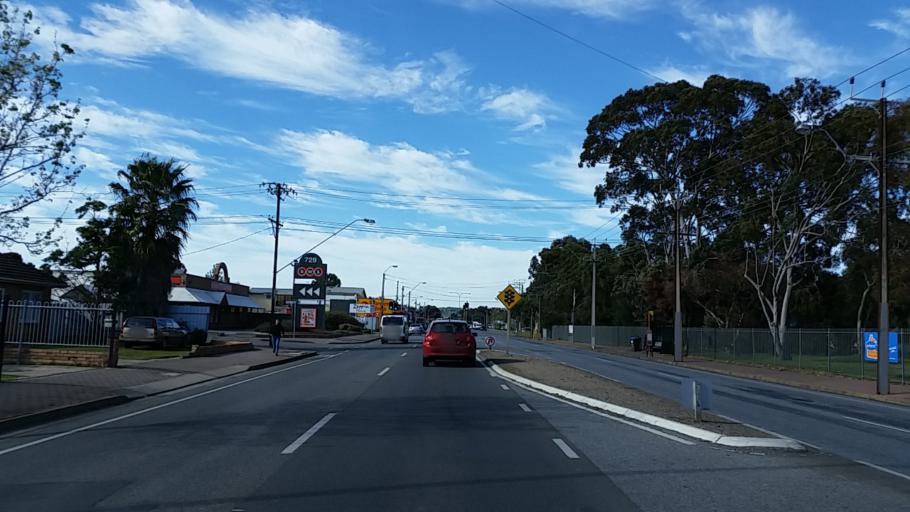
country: AU
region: South Australia
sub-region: Marion
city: South Plympton
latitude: -34.9899
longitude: 138.5568
